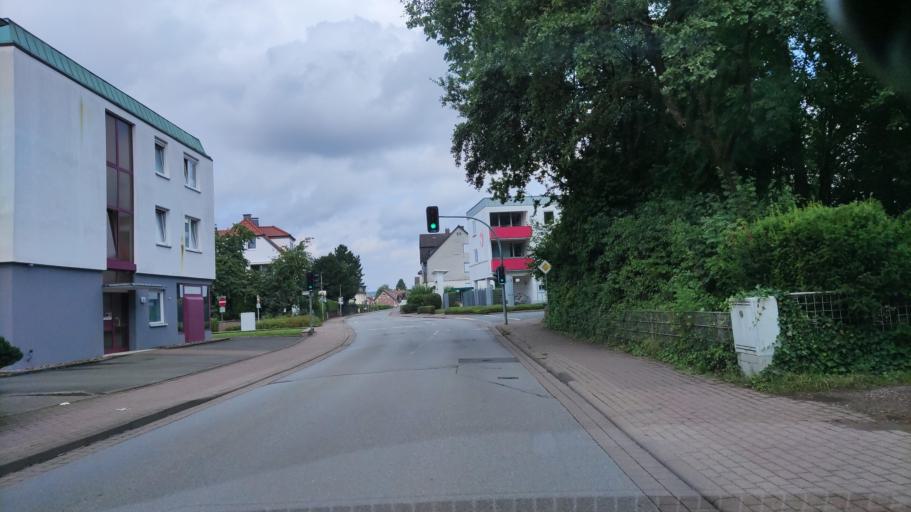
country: DE
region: Lower Saxony
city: Holzminden
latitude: 51.8257
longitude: 9.4676
